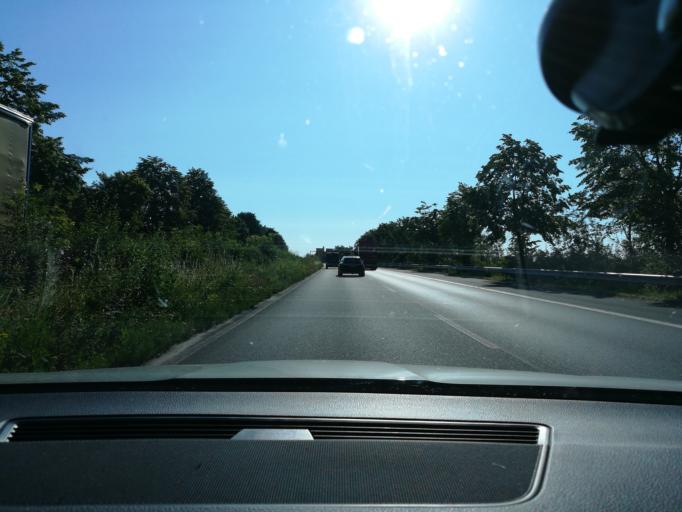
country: DE
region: North Rhine-Westphalia
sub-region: Regierungsbezirk Detmold
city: Minden
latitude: 52.2643
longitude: 8.8995
